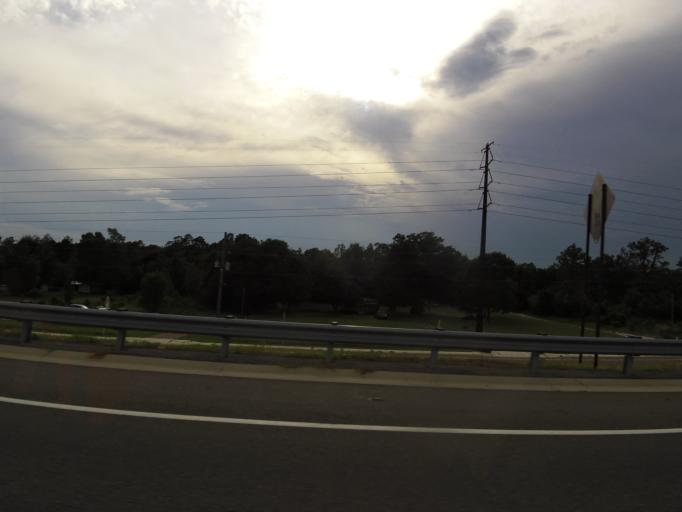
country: US
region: Florida
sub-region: Clay County
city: Lakeside
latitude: 30.1346
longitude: -81.8309
